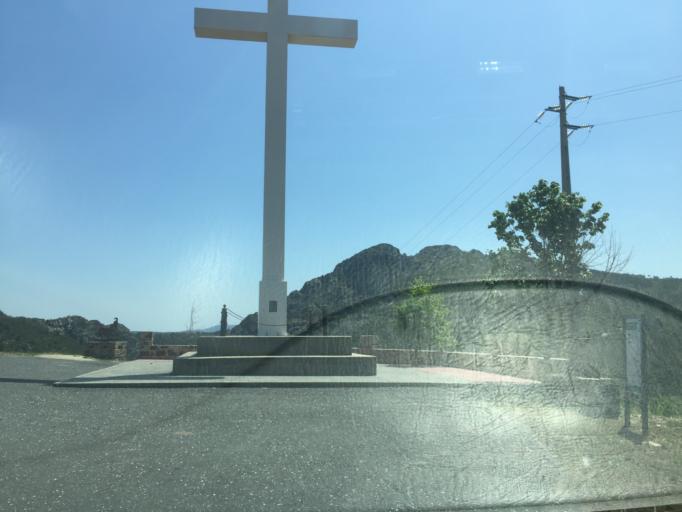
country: PT
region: Coimbra
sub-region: Pampilhosa da Serra
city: Pampilhosa da Serra
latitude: 40.0879
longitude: -7.8722
